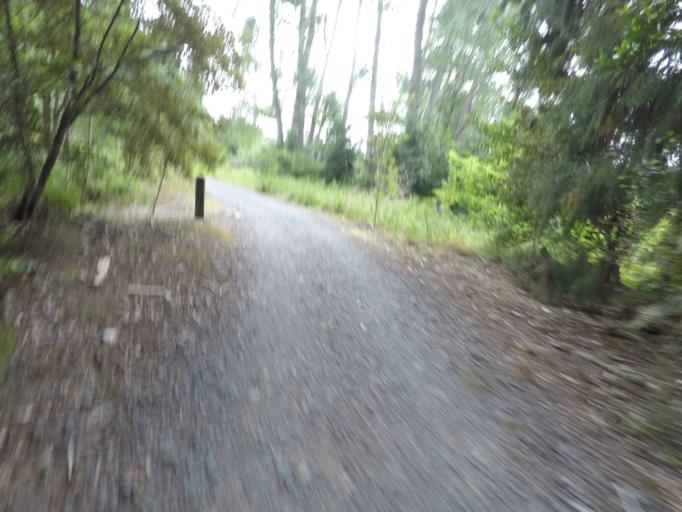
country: NZ
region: Northland
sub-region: Whangarei
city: Whangarei
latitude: -35.7143
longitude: 174.3304
